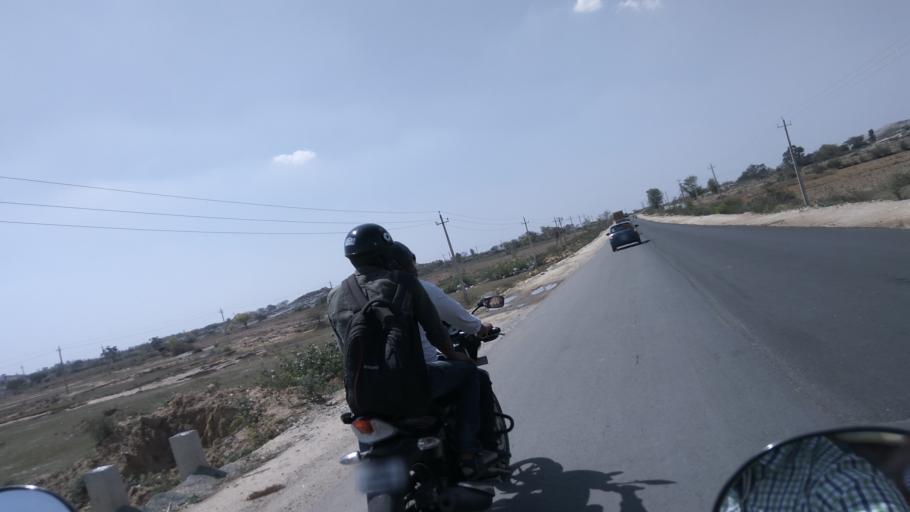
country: IN
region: Karnataka
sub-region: Kolar
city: Mulbagal
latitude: 13.1699
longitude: 78.3603
